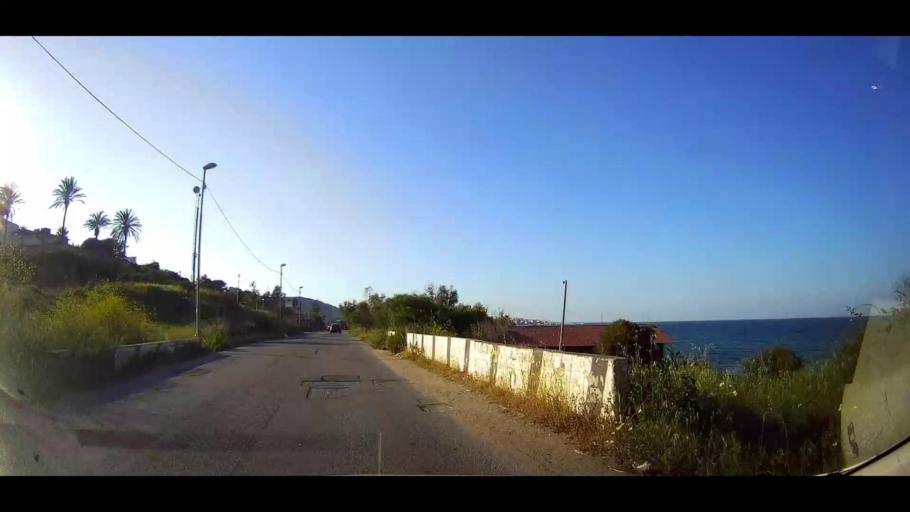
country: IT
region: Calabria
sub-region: Provincia di Crotone
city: Crotone
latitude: 39.0523
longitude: 17.1396
